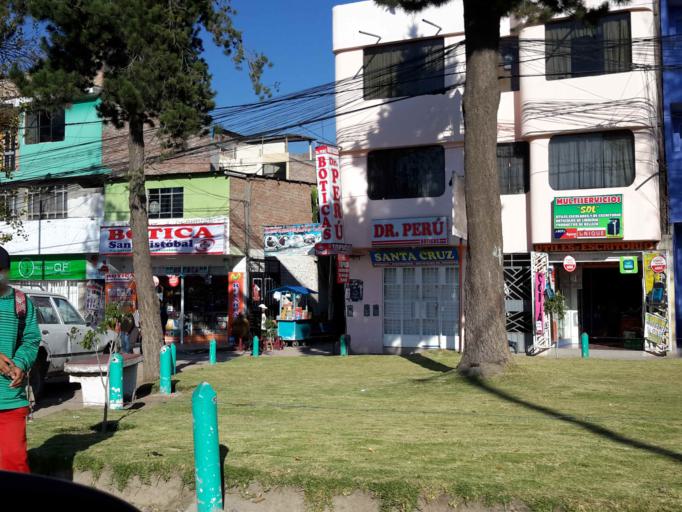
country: PE
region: Ayacucho
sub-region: Provincia de Huamanga
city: Ayacucho
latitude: -13.1520
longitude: -74.2233
